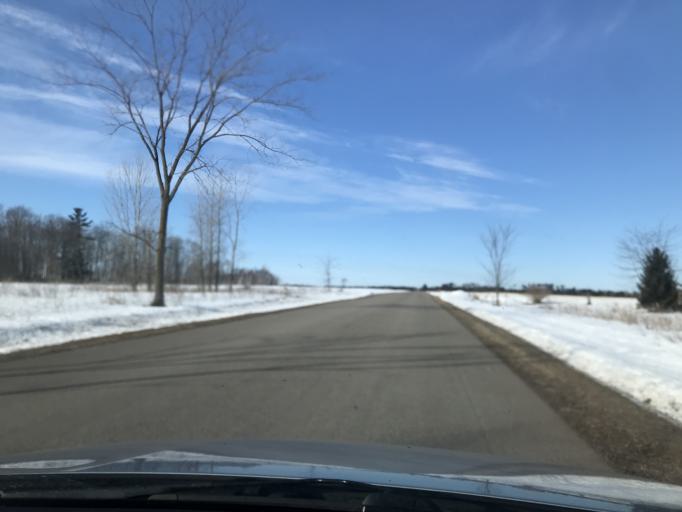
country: US
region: Wisconsin
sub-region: Oconto County
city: Oconto Falls
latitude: 44.9383
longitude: -88.1938
